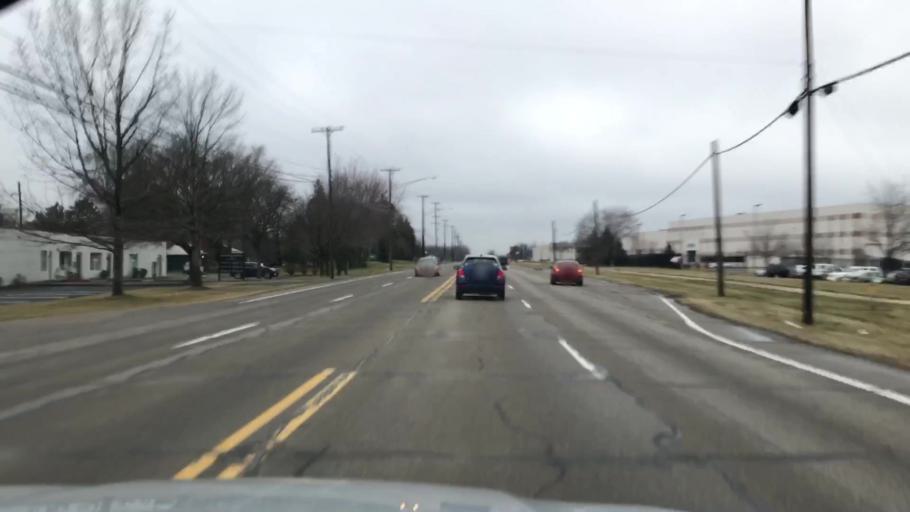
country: US
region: Michigan
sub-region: Wayne County
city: Westland
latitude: 42.3699
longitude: -83.4198
